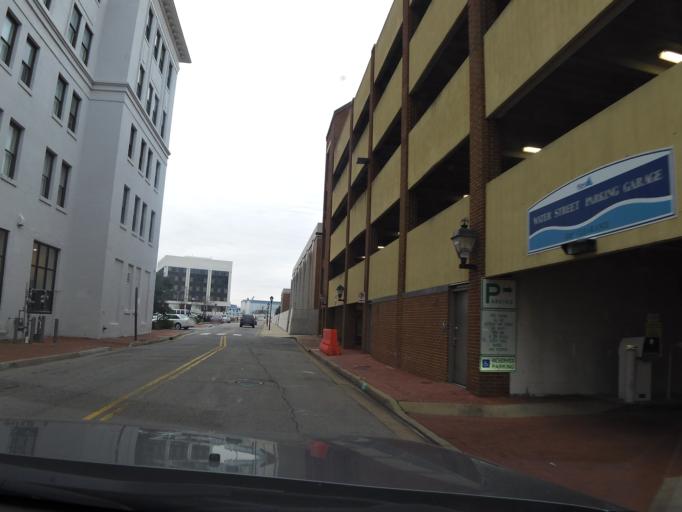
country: US
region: Virginia
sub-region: City of Portsmouth
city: Portsmouth
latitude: 36.8350
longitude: -76.2969
